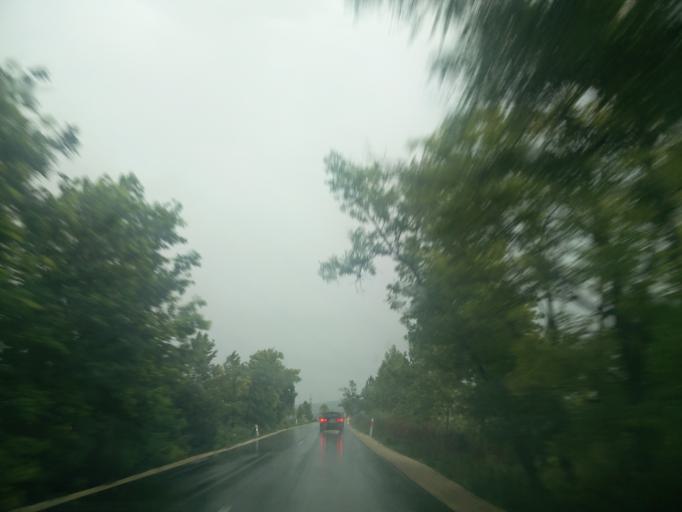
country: HU
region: Fejer
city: Etyek
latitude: 47.4555
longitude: 18.7817
